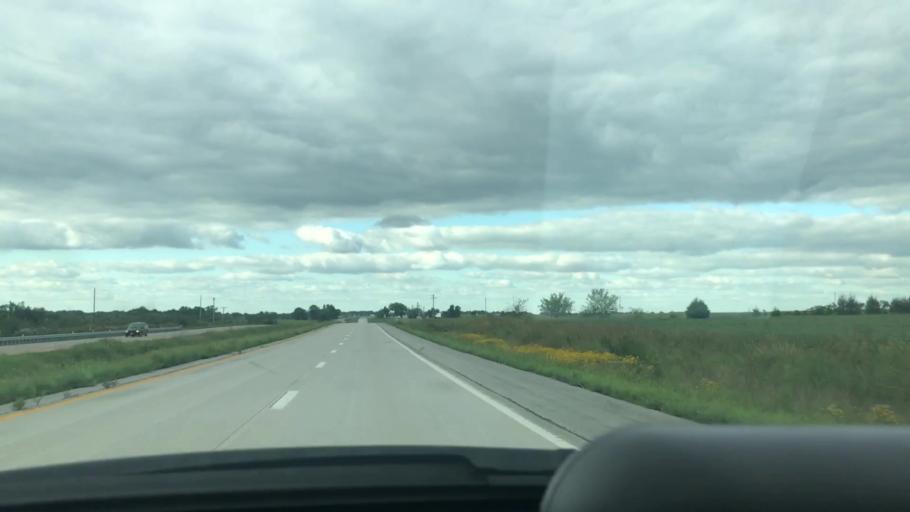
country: US
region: Missouri
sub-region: Benton County
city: Lincoln
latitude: 38.3591
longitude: -93.3392
